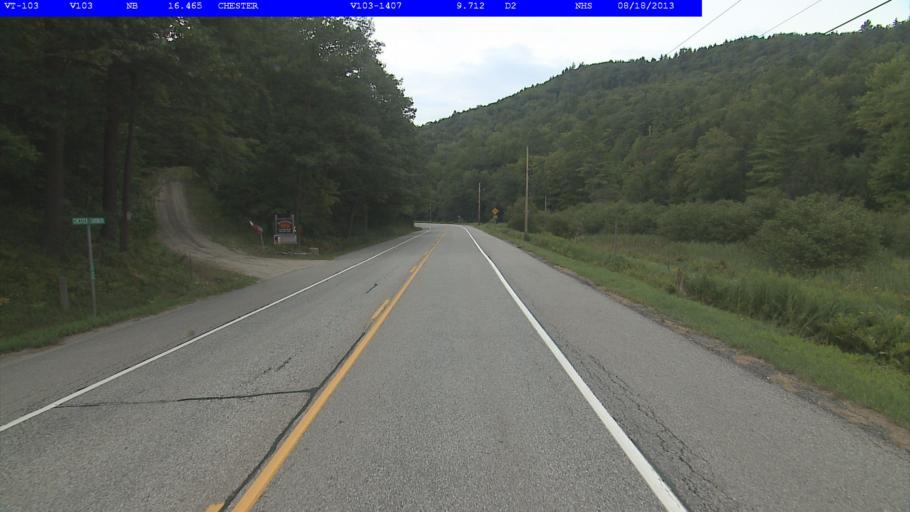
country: US
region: Vermont
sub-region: Windsor County
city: Chester
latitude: 43.3491
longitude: -72.6255
